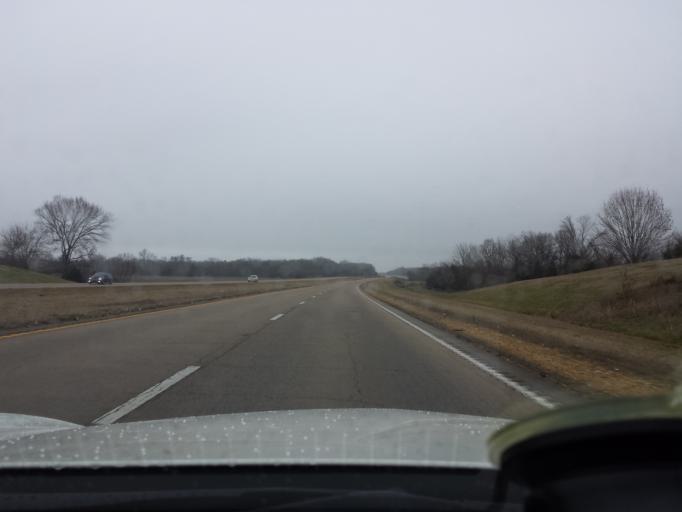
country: US
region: Mississippi
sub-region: Lee County
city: Shannon
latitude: 34.0712
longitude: -88.7031
